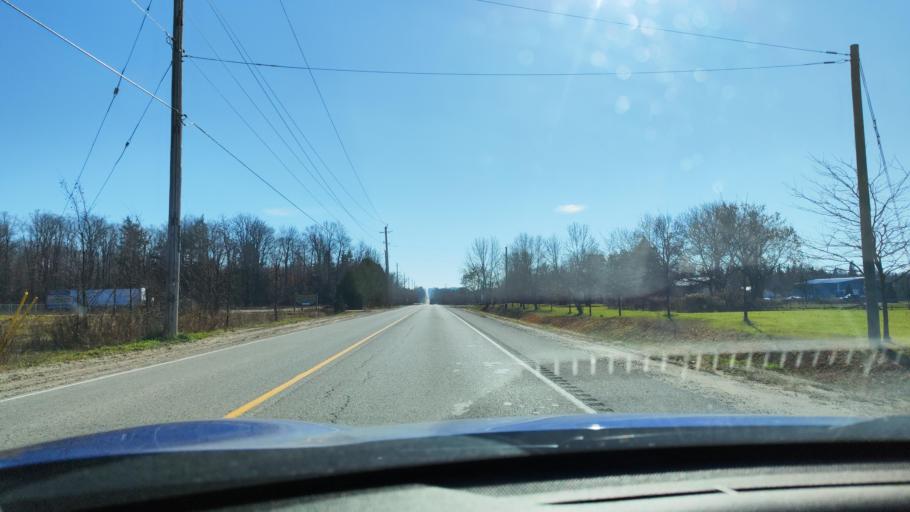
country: CA
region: Ontario
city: Wasaga Beach
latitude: 44.4797
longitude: -80.0082
